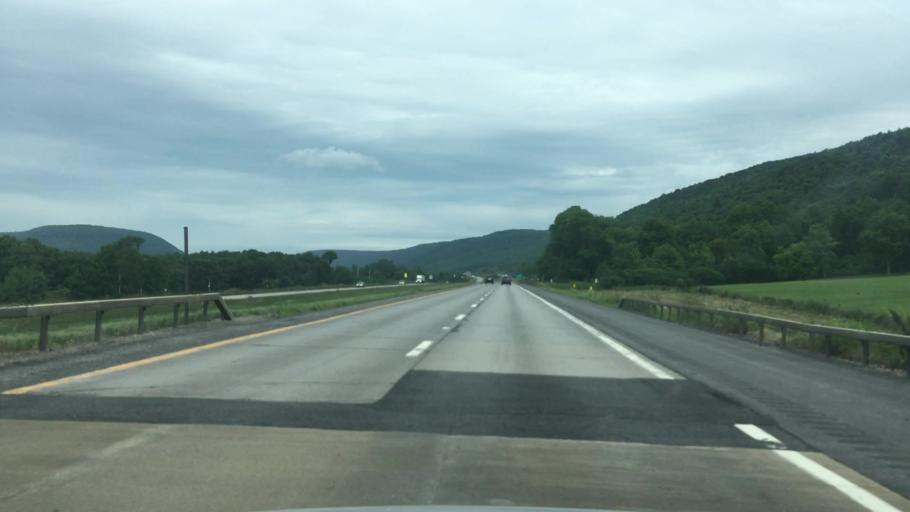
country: US
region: New York
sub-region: Otsego County
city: Worcester
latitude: 42.5358
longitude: -74.8467
